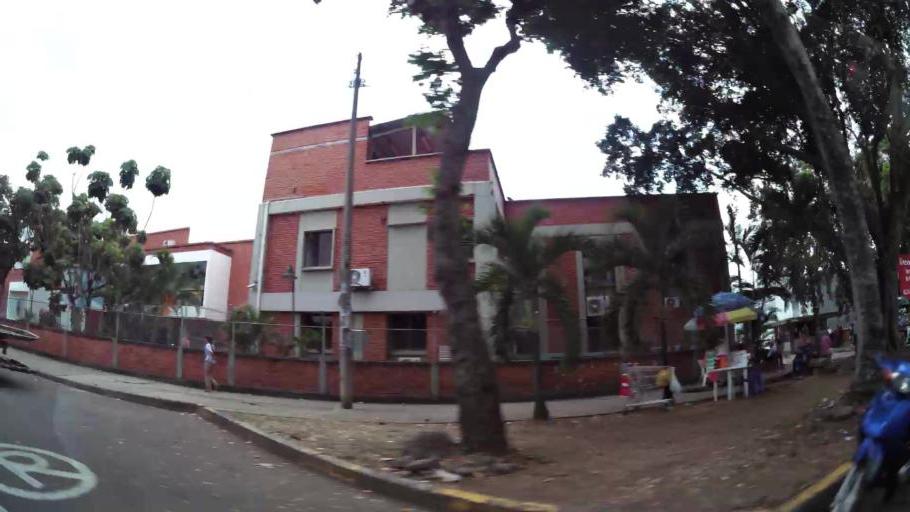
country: CO
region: Valle del Cauca
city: Cali
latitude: 3.4669
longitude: -76.4969
